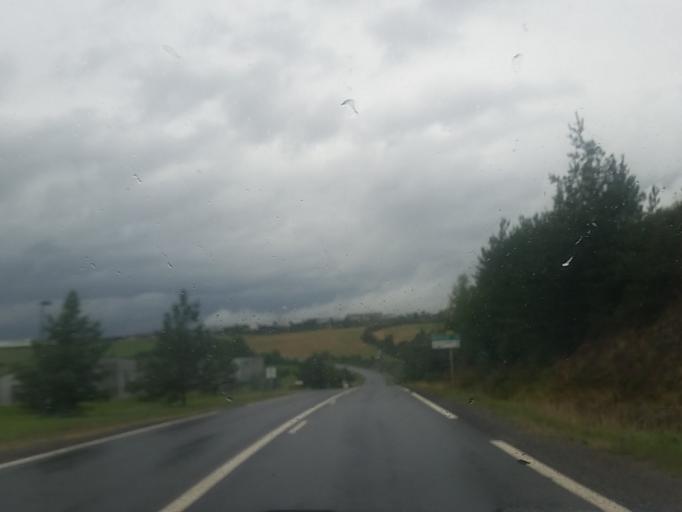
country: FR
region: Auvergne
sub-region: Departement du Cantal
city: Saint-Flour
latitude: 45.0290
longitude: 3.0638
